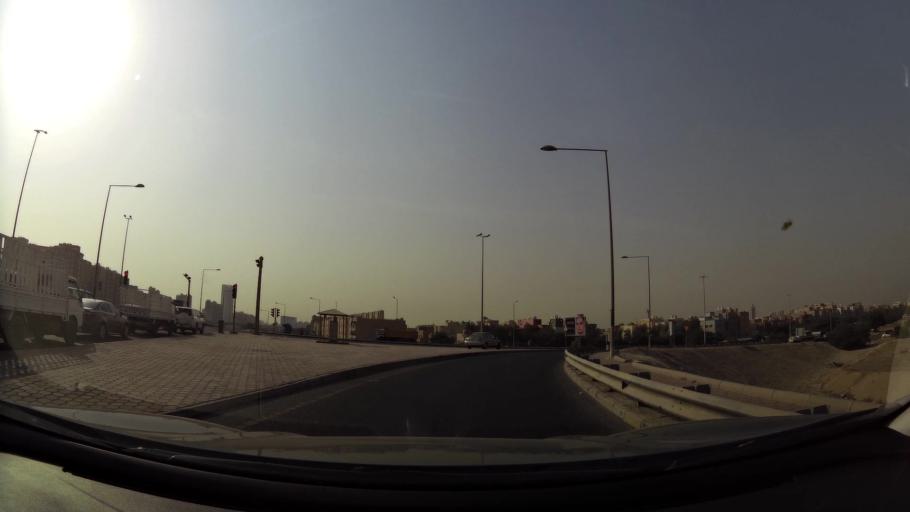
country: KW
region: Al Ahmadi
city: Al Fintas
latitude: 29.1844
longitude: 48.1114
